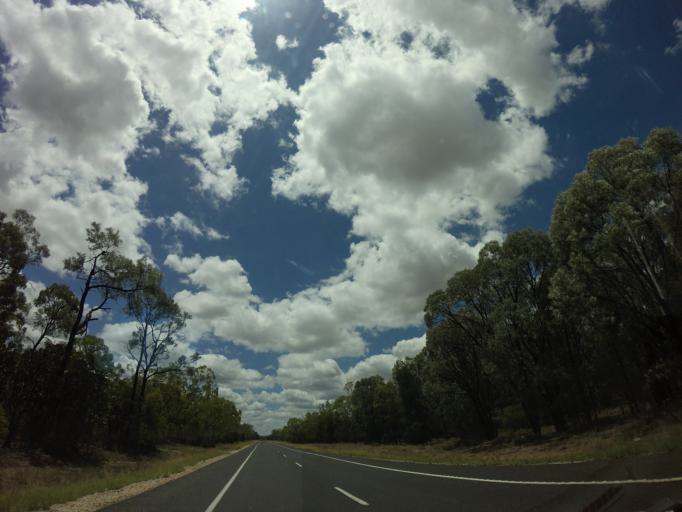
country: AU
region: Queensland
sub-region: Goondiwindi
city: Goondiwindi
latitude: -28.1038
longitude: 150.7227
